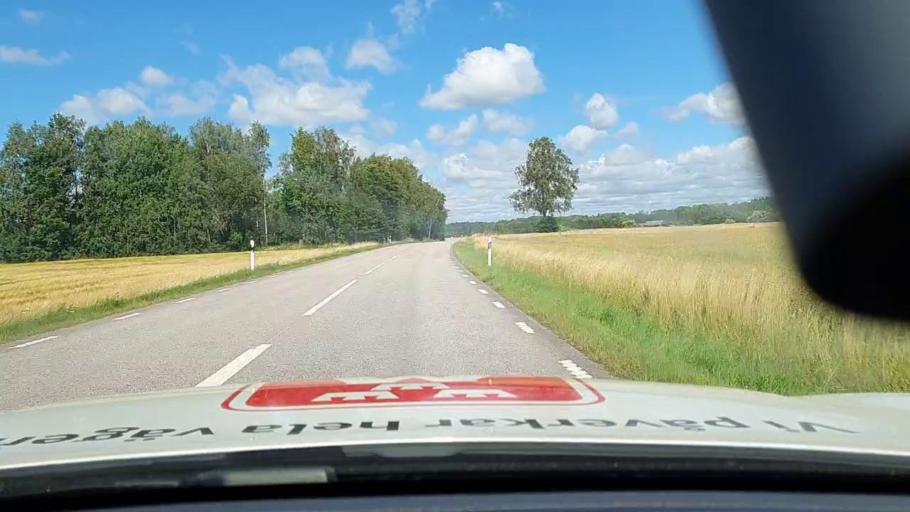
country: SE
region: Vaestra Goetaland
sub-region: Skovde Kommun
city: Stopen
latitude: 58.4891
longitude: 13.9610
